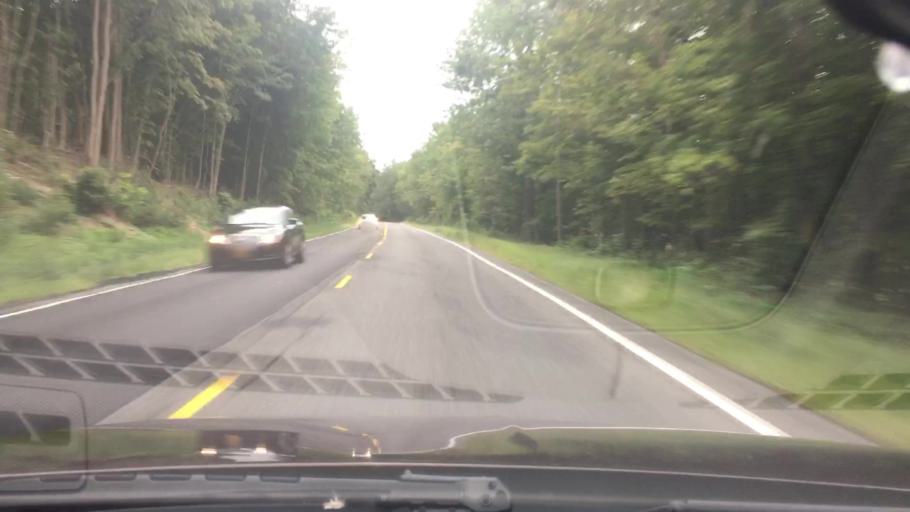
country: US
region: New York
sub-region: Dutchess County
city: Millbrook
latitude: 41.7885
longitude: -73.7260
